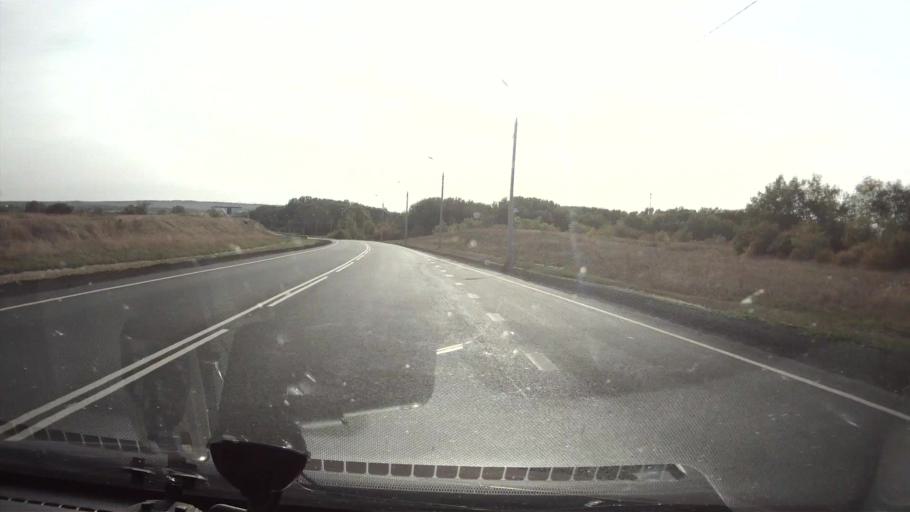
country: RU
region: Saratov
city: Yelshanka
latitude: 51.8284
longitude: 46.2253
